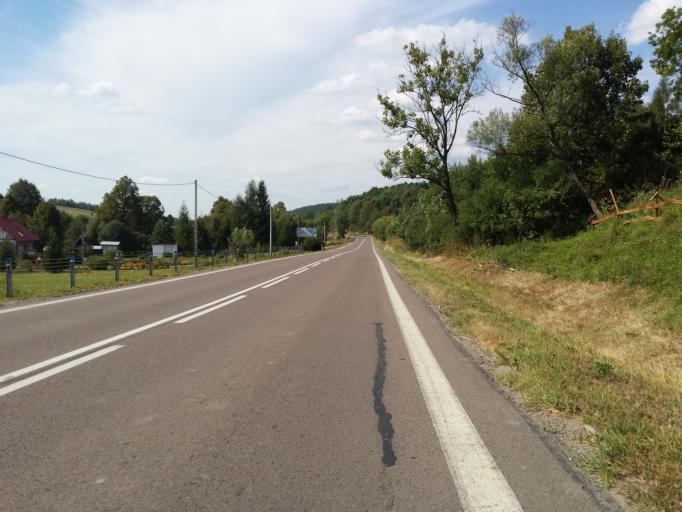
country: PL
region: Subcarpathian Voivodeship
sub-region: Powiat bieszczadzki
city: Ustrzyki Dolne
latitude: 49.5438
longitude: 22.5860
